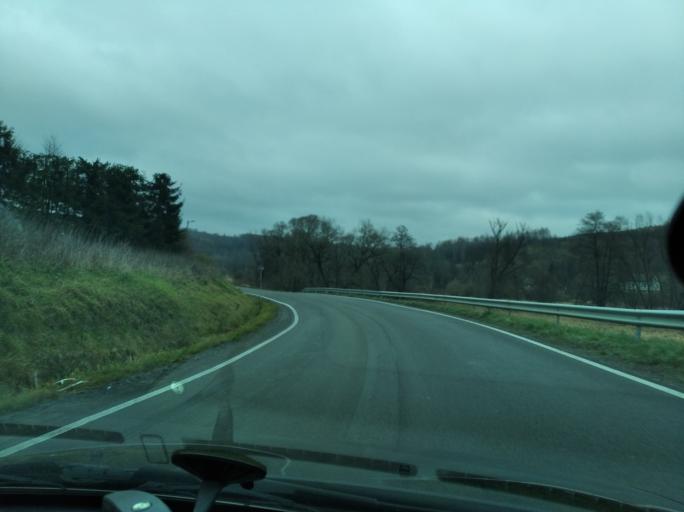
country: PL
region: Subcarpathian Voivodeship
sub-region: Powiat przeworski
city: Jawornik Polski
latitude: 49.9166
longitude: 22.3024
